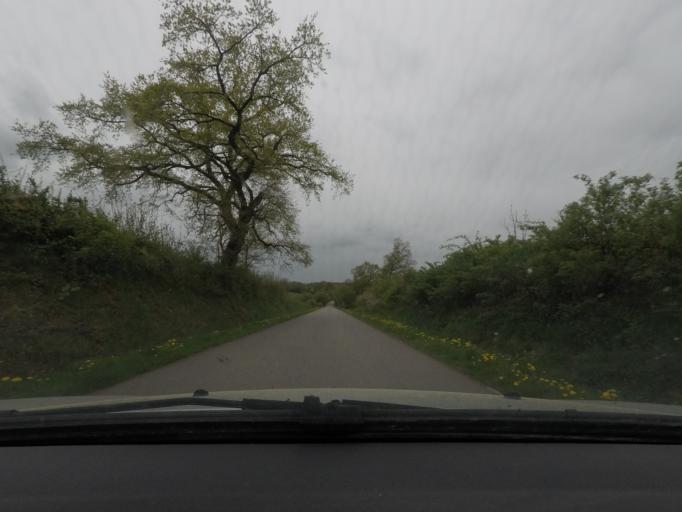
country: BE
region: Wallonia
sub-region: Province du Luxembourg
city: Etalle
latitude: 49.7161
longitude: 5.5663
